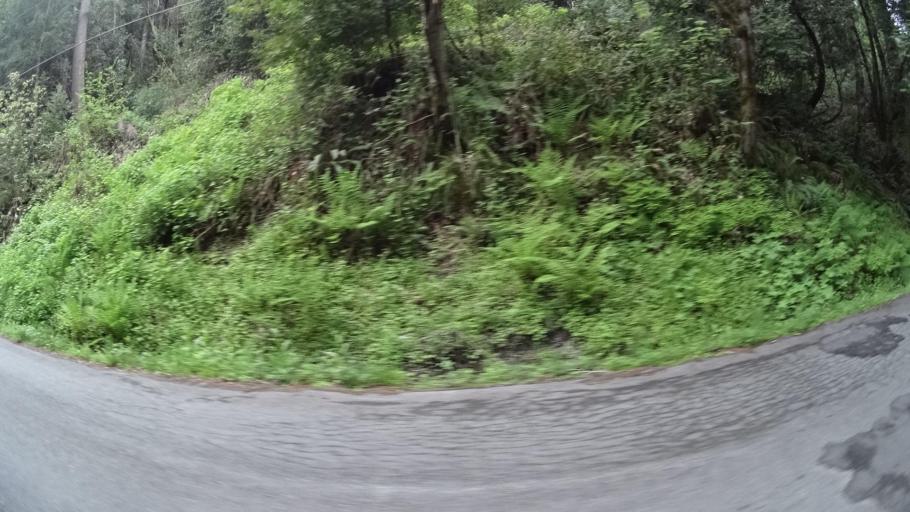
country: US
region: California
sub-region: Humboldt County
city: Blue Lake
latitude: 40.9594
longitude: -123.8380
